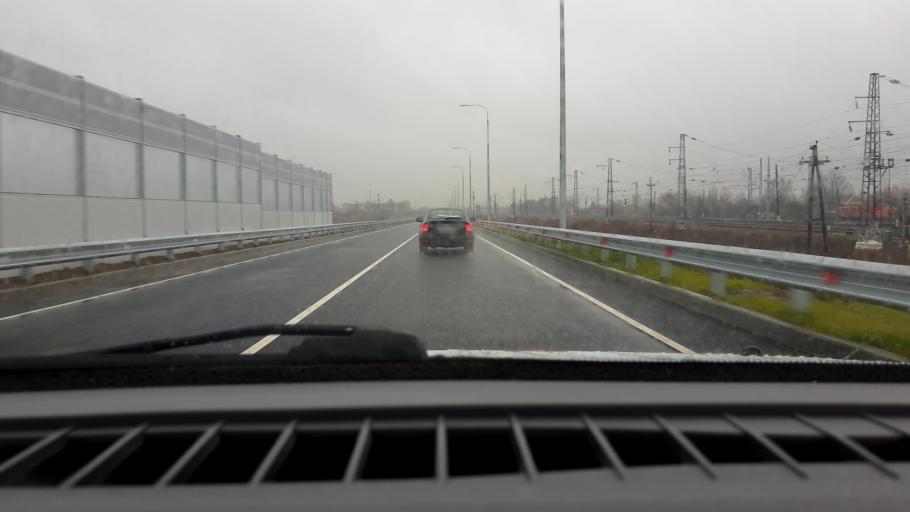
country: RU
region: Nizjnij Novgorod
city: Neklyudovo
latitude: 56.4145
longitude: 43.9834
